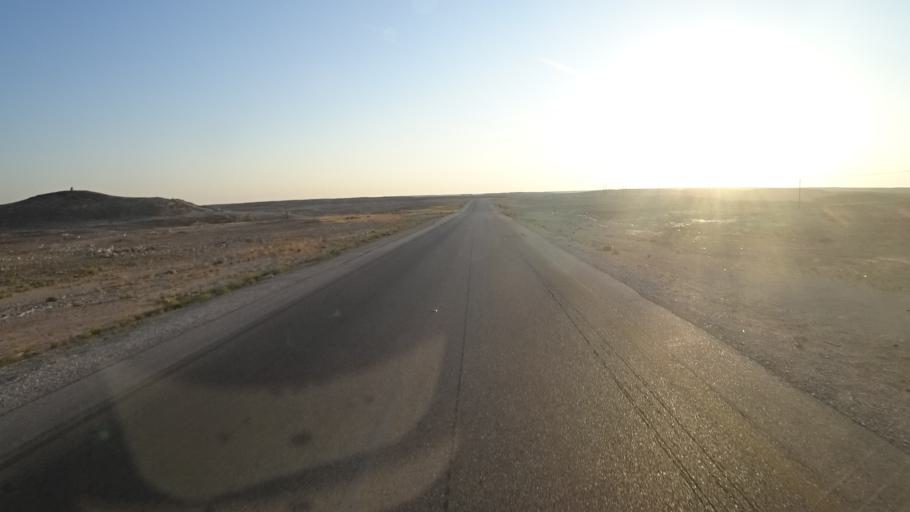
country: OM
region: Zufar
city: Salalah
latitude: 17.5298
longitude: 53.4007
